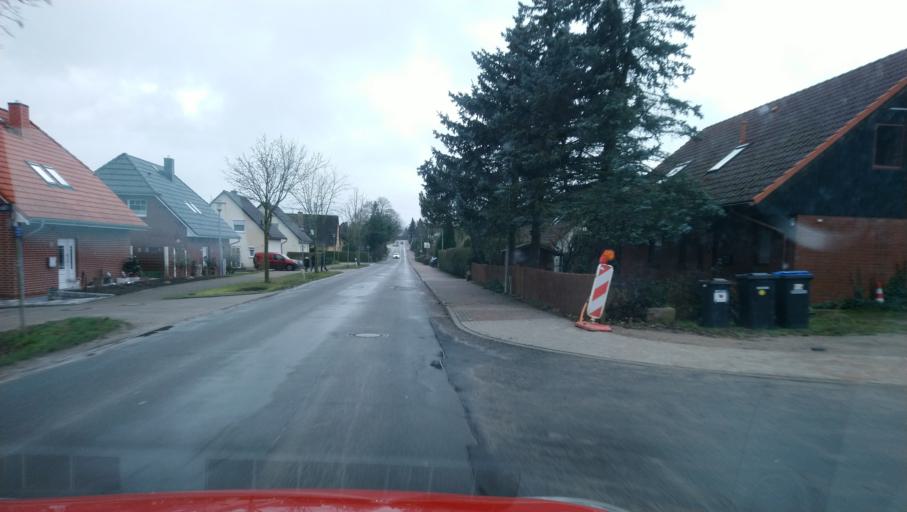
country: DE
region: Mecklenburg-Vorpommern
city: Seehof
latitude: 53.6825
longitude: 11.4292
